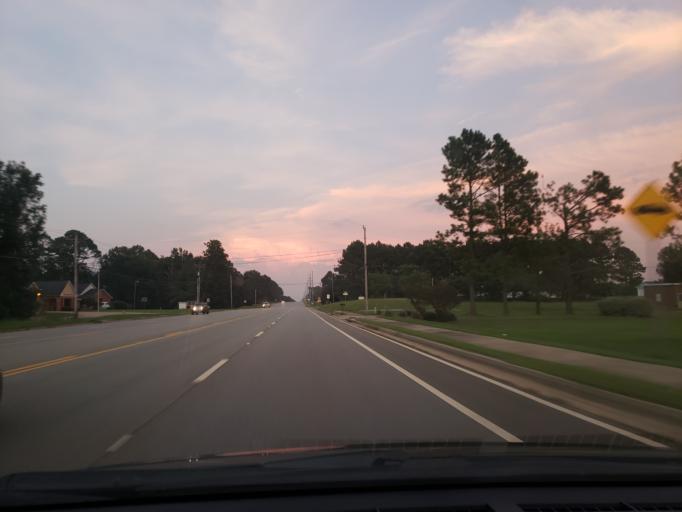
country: US
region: Georgia
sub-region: Dougherty County
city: Albany
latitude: 31.5856
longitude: -84.2854
